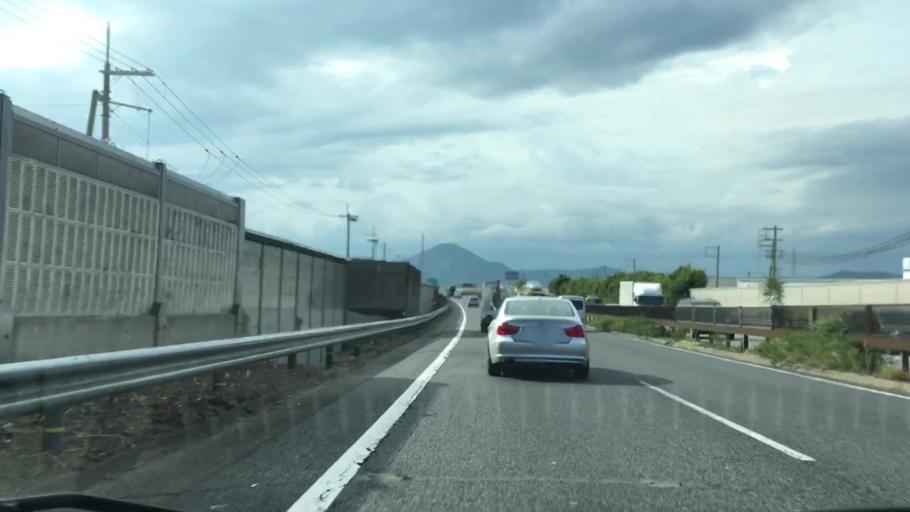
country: JP
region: Hyogo
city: Kakogawacho-honmachi
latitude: 34.7801
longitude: 134.8342
